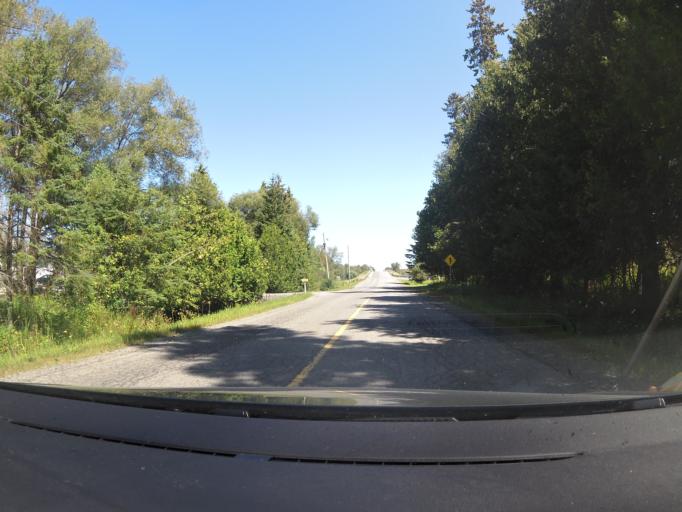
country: CA
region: Ontario
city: Bells Corners
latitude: 45.2949
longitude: -76.0274
